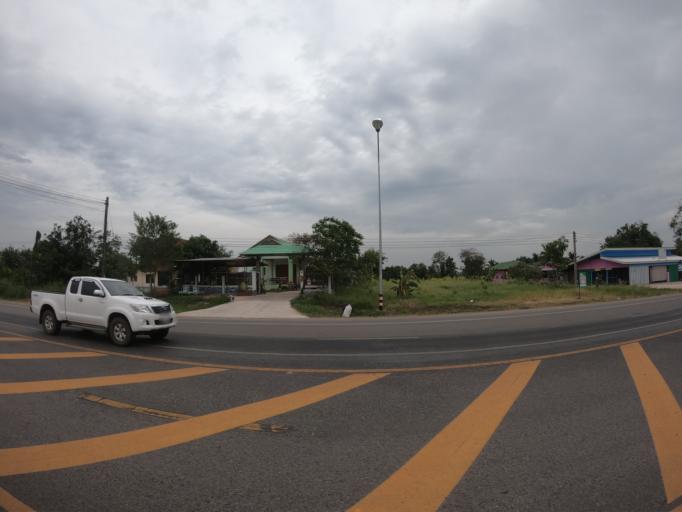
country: TH
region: Roi Et
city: Chiang Khwan
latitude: 16.1286
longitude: 103.8487
